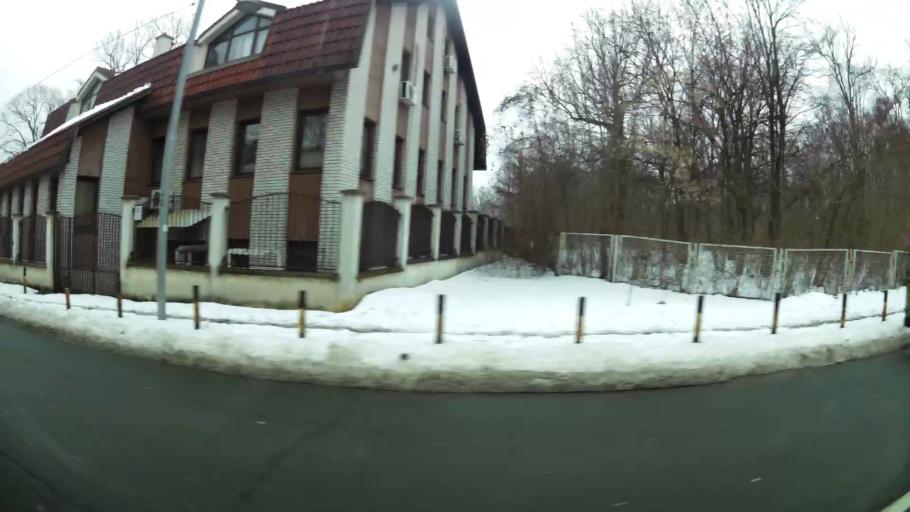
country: RS
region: Central Serbia
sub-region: Belgrade
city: Vozdovac
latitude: 44.7678
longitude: 20.4670
